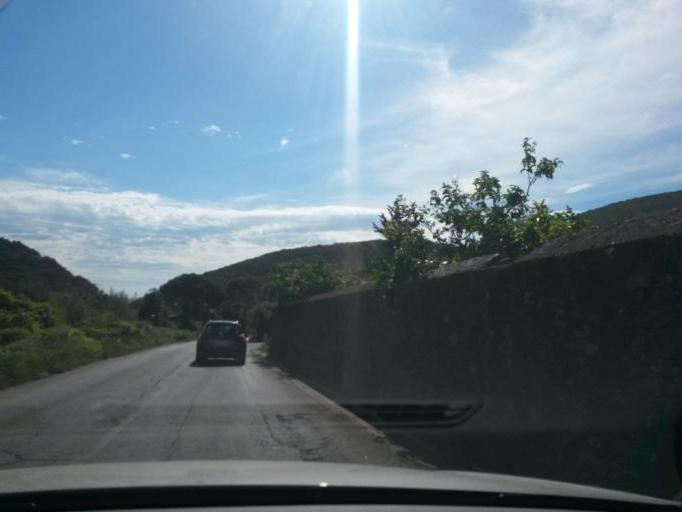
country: IT
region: Tuscany
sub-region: Provincia di Livorno
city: Rio nell'Elba
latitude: 42.8126
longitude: 10.4105
